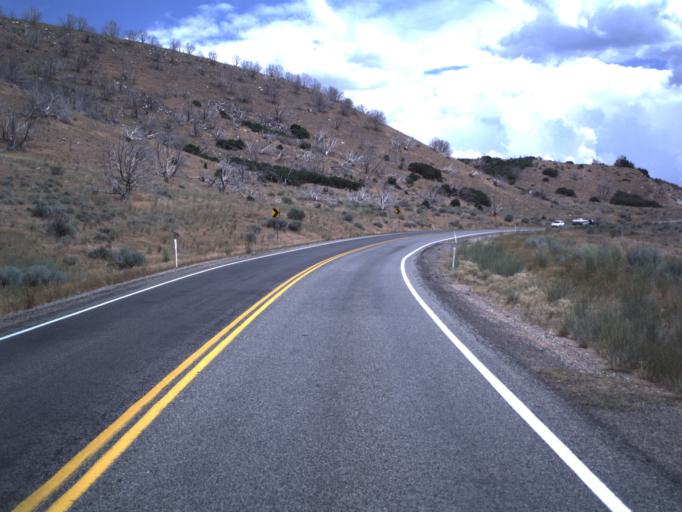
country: US
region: Utah
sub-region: Sanpete County
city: Fountain Green
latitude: 39.7022
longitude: -111.7014
